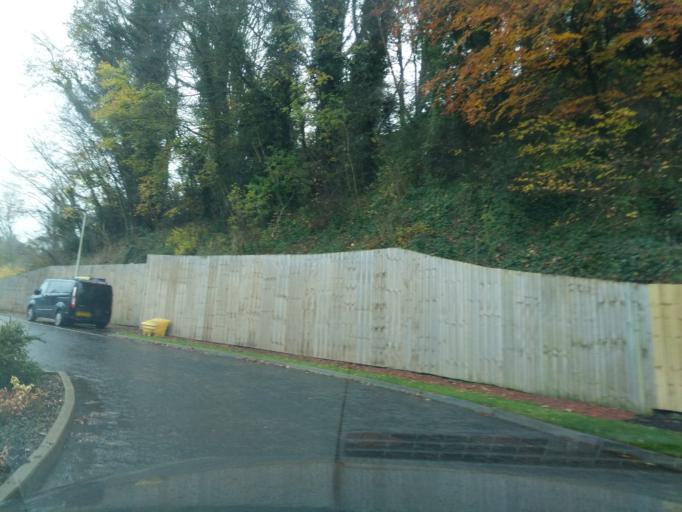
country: GB
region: Scotland
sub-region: Midlothian
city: Bonnyrigg
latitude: 55.8804
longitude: -3.1179
